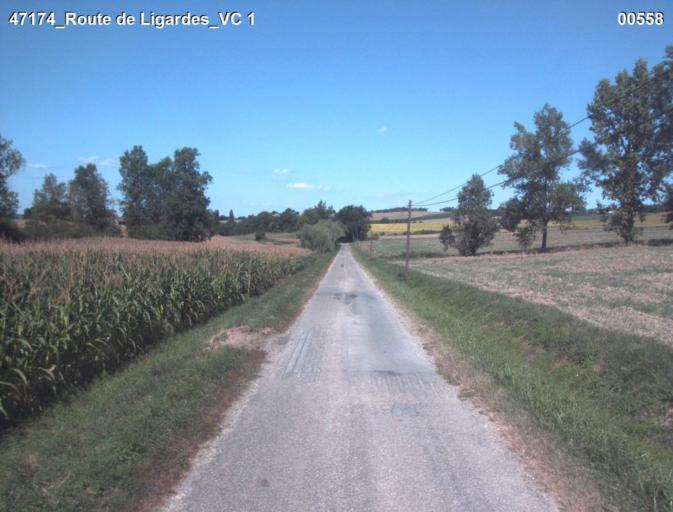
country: FR
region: Midi-Pyrenees
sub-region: Departement du Gers
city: Condom
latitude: 44.0298
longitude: 0.4119
